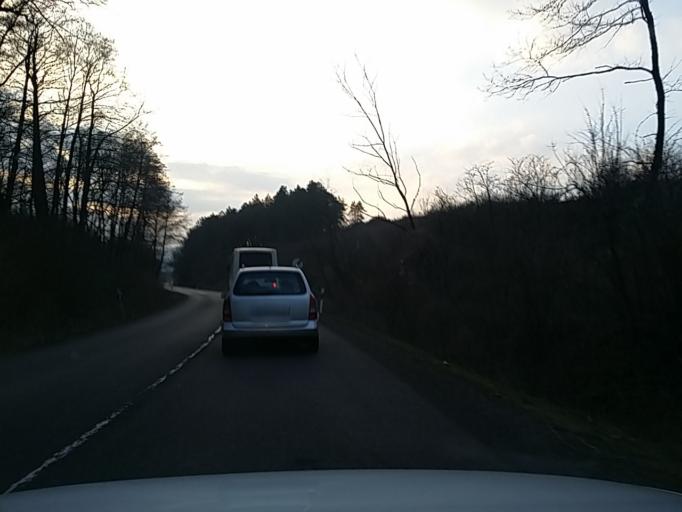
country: HU
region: Nograd
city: Matranovak
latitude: 48.0101
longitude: 19.9860
